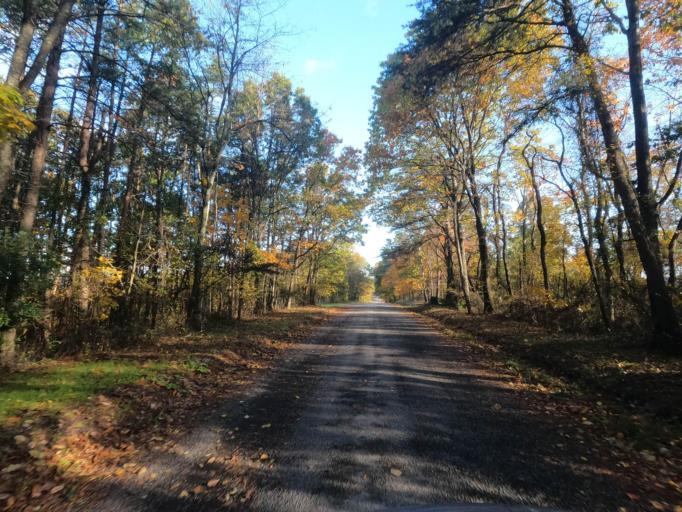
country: US
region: West Virginia
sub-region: Morgan County
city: Berkeley Springs
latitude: 39.6159
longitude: -78.4901
